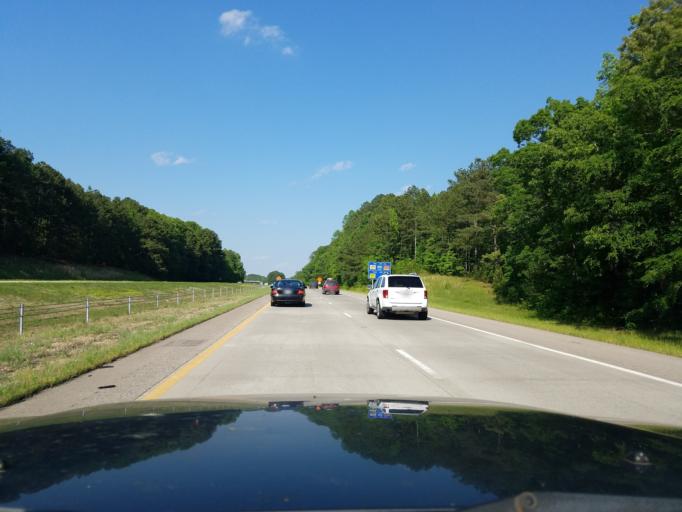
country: US
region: North Carolina
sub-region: Vance County
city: South Henderson
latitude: 36.3222
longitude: -78.4591
